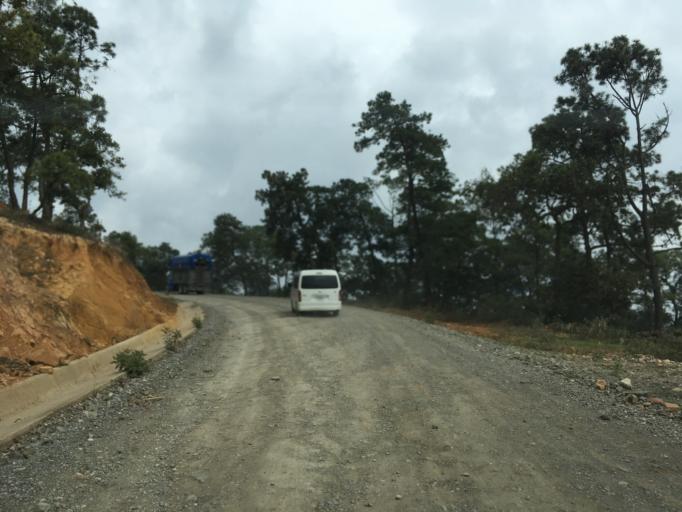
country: MX
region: Oaxaca
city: Santiago Tilantongo
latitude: 17.2083
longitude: -97.2770
